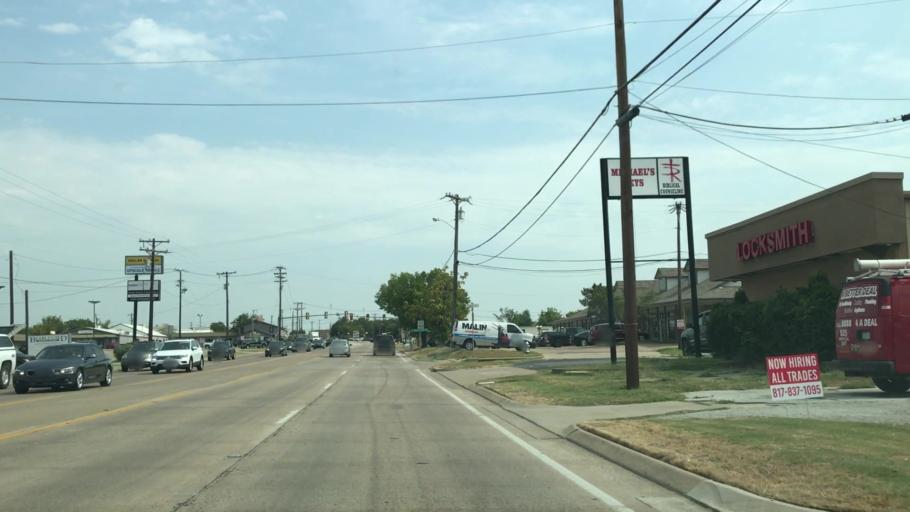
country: US
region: Texas
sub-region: Tarrant County
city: Keller
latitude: 32.9370
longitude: -97.2534
